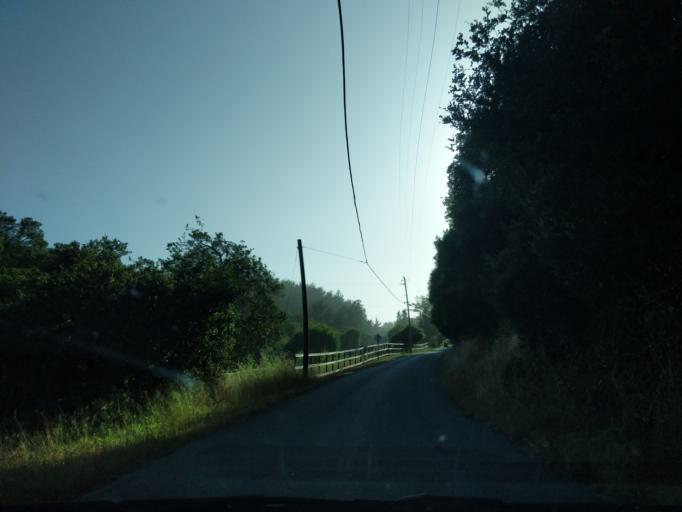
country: US
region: California
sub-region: Monterey County
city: Las Lomas
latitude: 36.8933
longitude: -121.7019
